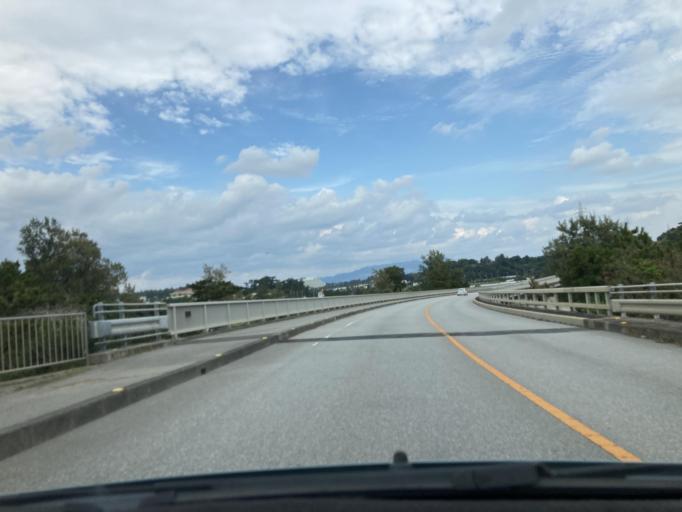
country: JP
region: Okinawa
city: Ishikawa
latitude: 26.4911
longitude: 127.8536
